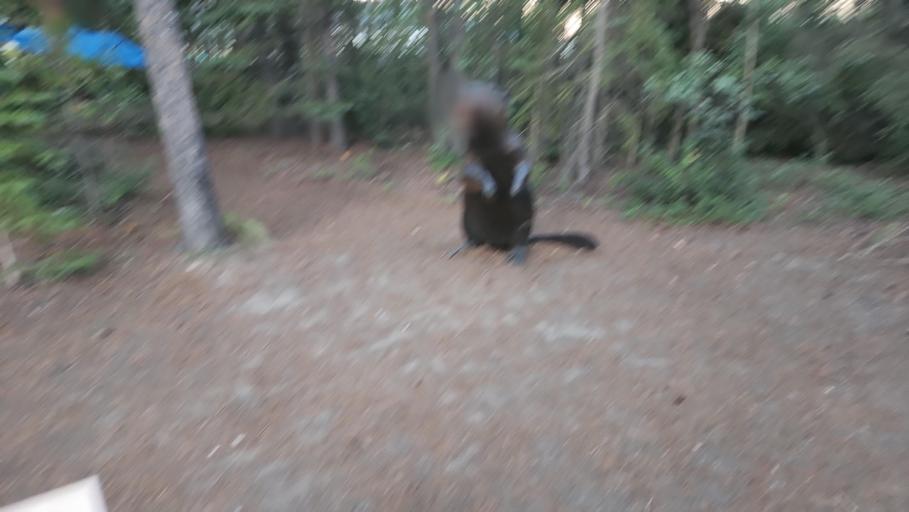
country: CA
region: Yukon
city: Whitehorse
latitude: 60.7096
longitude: -135.0791
